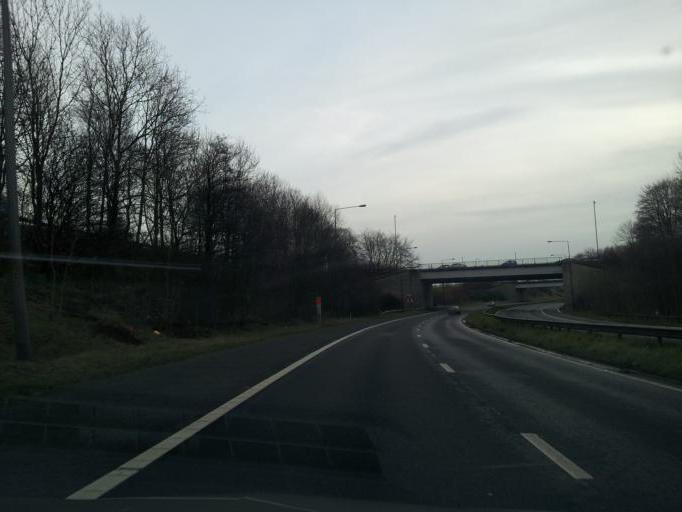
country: GB
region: England
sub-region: Borough of Oldham
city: Royton
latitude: 53.5583
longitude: -2.1407
